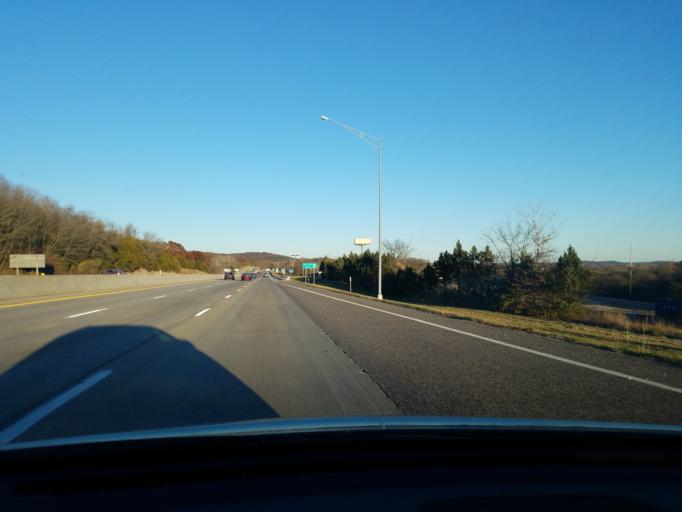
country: US
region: Missouri
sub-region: Franklin County
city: Gray Summit
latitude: 38.4850
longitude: -90.8160
